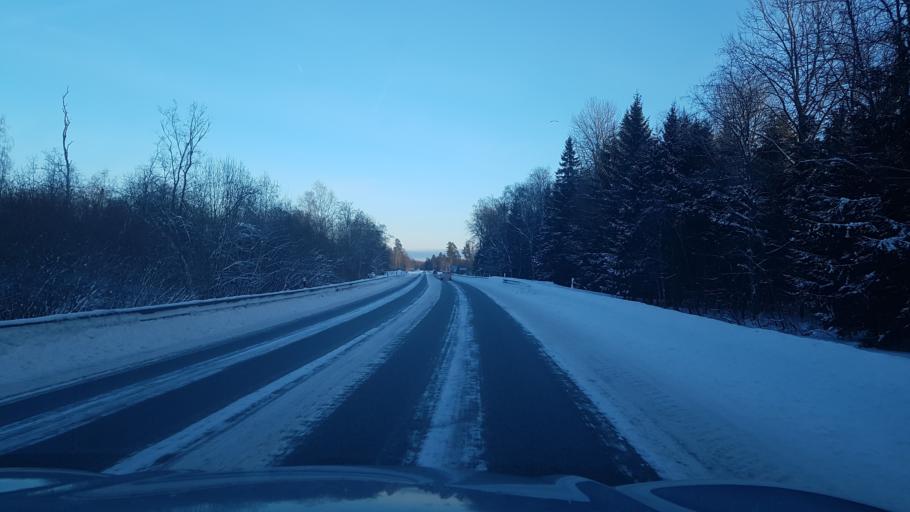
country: EE
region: Ida-Virumaa
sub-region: Toila vald
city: Toila
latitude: 59.3738
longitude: 27.5025
